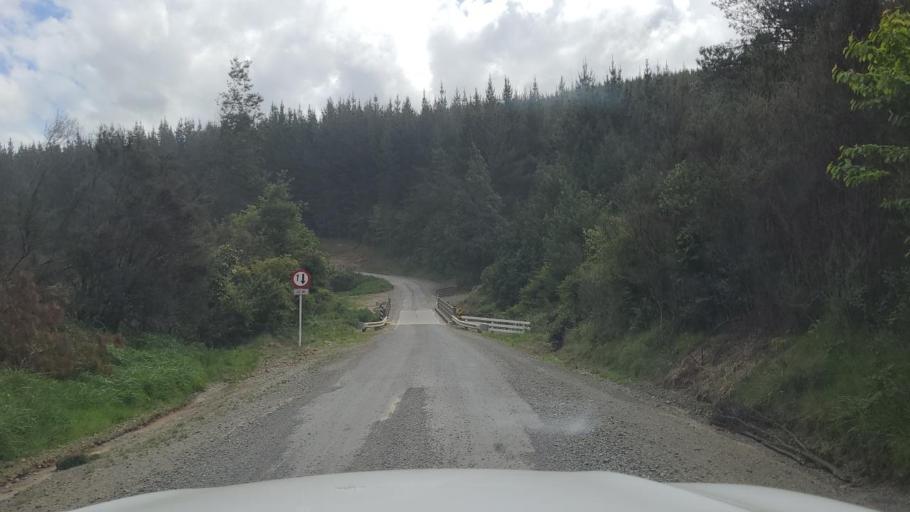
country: NZ
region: Hawke's Bay
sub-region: Napier City
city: Taradale
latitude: -39.2738
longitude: 176.6722
